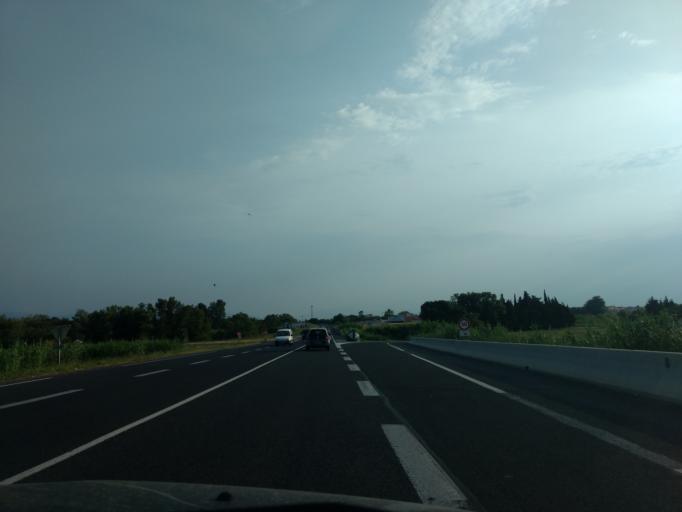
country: FR
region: Languedoc-Roussillon
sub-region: Departement des Pyrenees-Orientales
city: Canet-en-Roussillon
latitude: 42.7097
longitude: 3.0219
